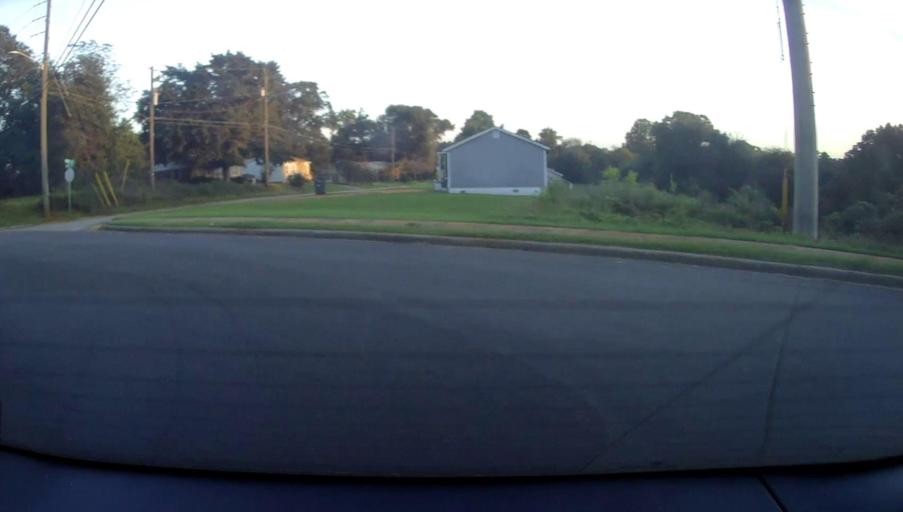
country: US
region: Georgia
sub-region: Houston County
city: Perry
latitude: 32.4647
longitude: -83.7400
